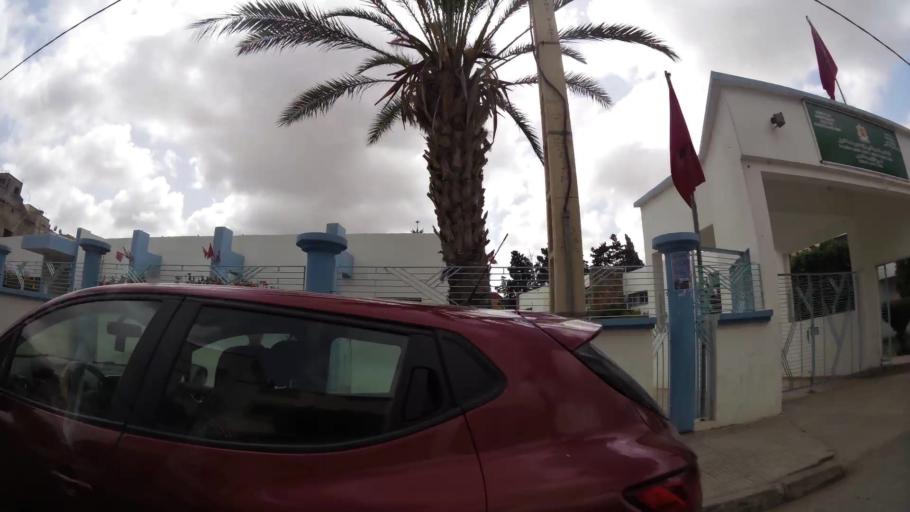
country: MA
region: Oriental
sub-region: Nador
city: Nador
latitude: 35.1744
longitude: -2.9309
